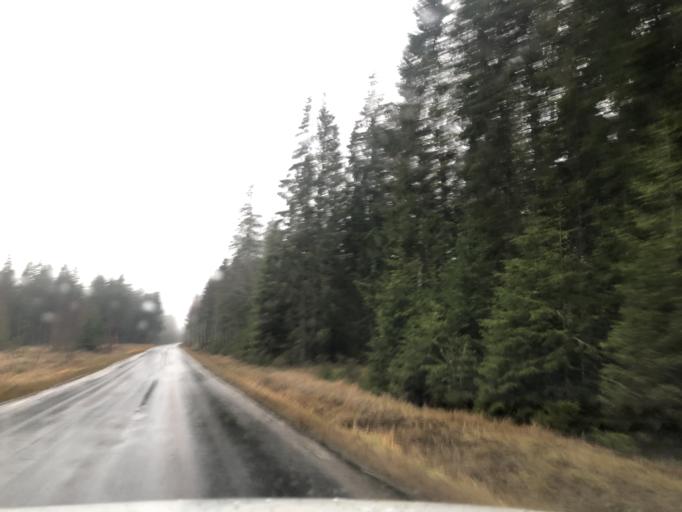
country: SE
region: Vaestra Goetaland
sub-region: Ulricehamns Kommun
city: Ulricehamn
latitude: 57.8401
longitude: 13.5365
